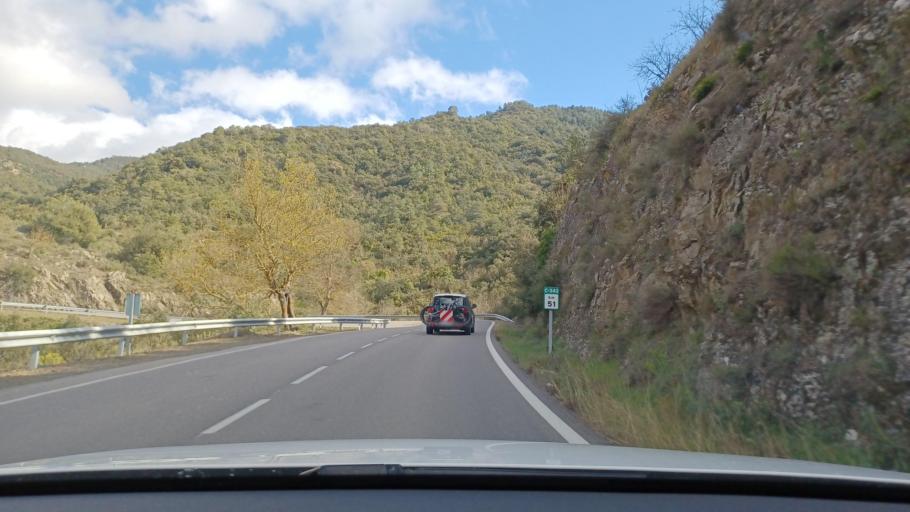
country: ES
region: Catalonia
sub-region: Provincia de Tarragona
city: Alforja
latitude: 41.2247
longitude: 0.9076
